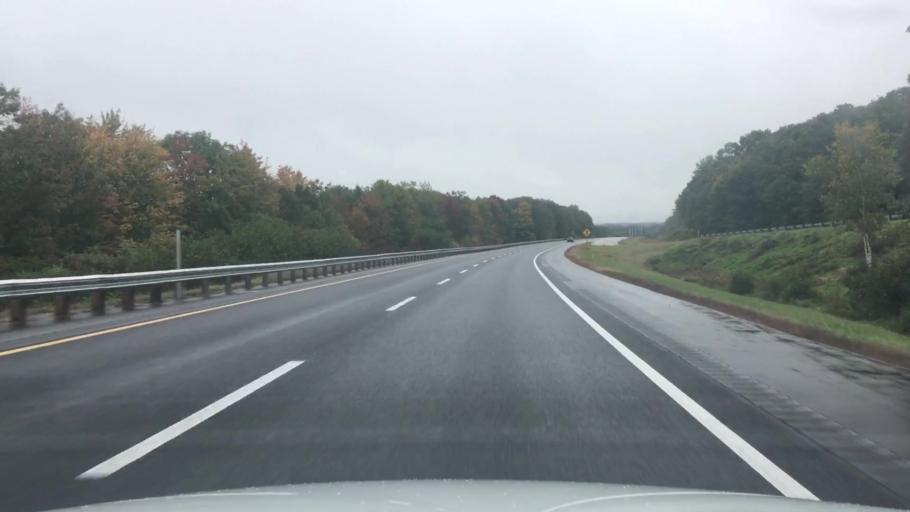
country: US
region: Maine
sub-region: Kennebec County
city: Gardiner
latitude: 44.1820
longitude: -69.8327
